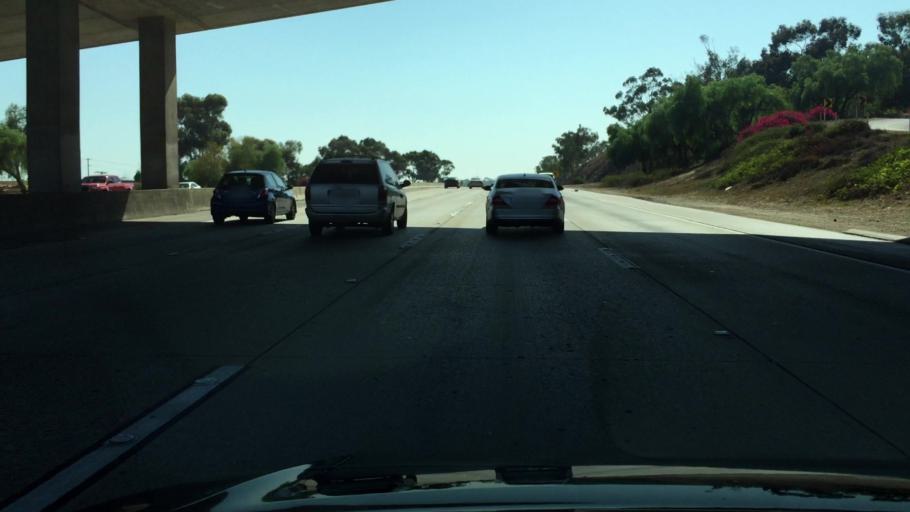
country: US
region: California
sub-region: San Diego County
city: Lemon Grove
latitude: 32.7465
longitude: -117.0312
